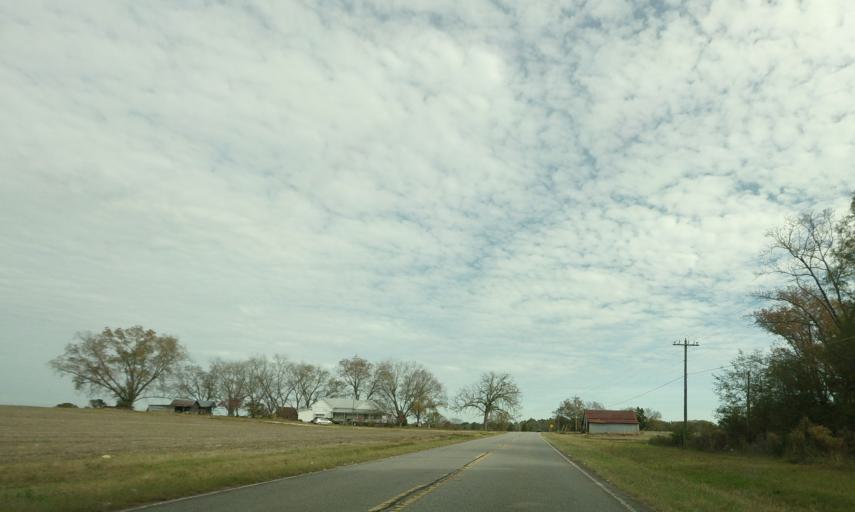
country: US
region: Georgia
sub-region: Bleckley County
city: Cochran
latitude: 32.3963
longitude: -83.2710
